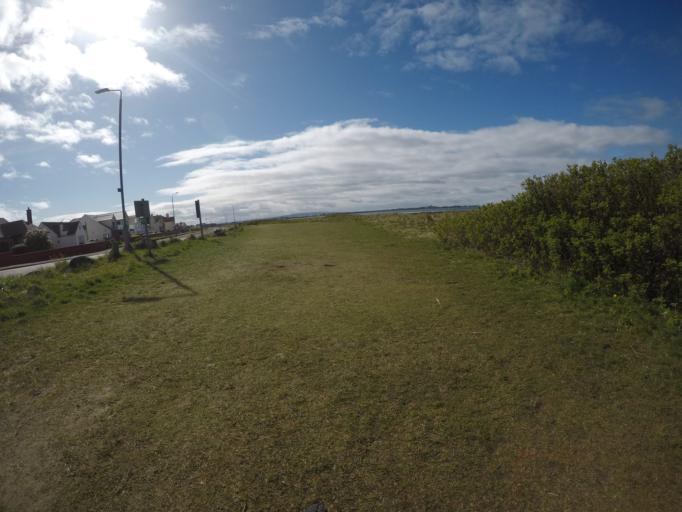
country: GB
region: Scotland
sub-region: South Ayrshire
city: Troon
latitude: 55.5663
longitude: -4.6583
